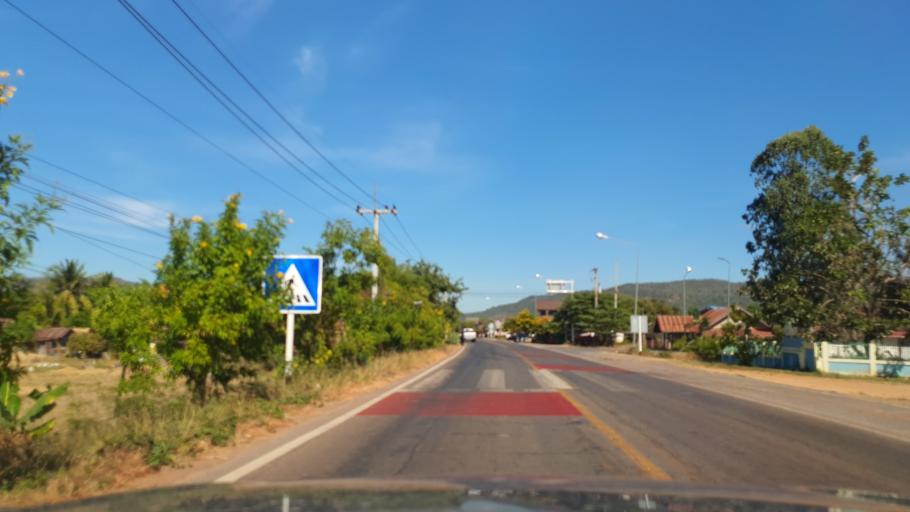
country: TH
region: Kalasin
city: Khao Wong
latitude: 16.7331
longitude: 104.0952
